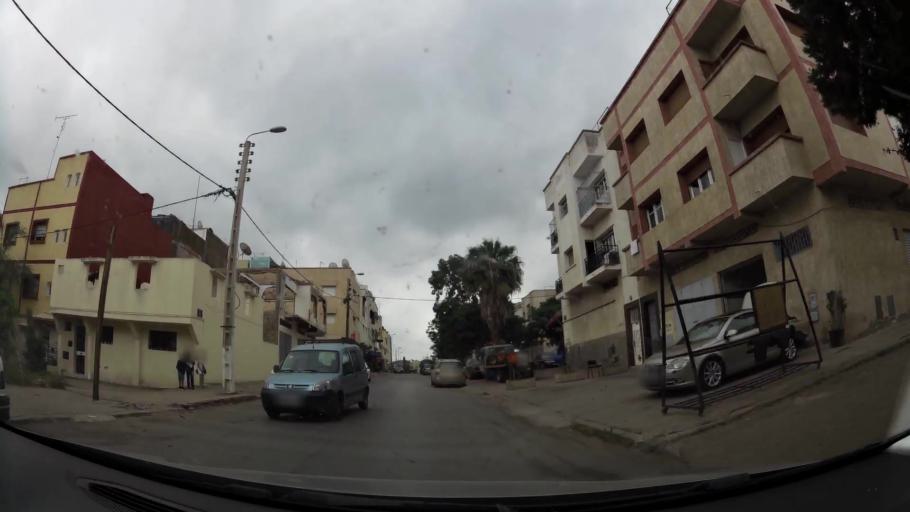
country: MA
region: Rabat-Sale-Zemmour-Zaer
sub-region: Rabat
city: Rabat
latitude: 33.9804
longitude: -6.8154
